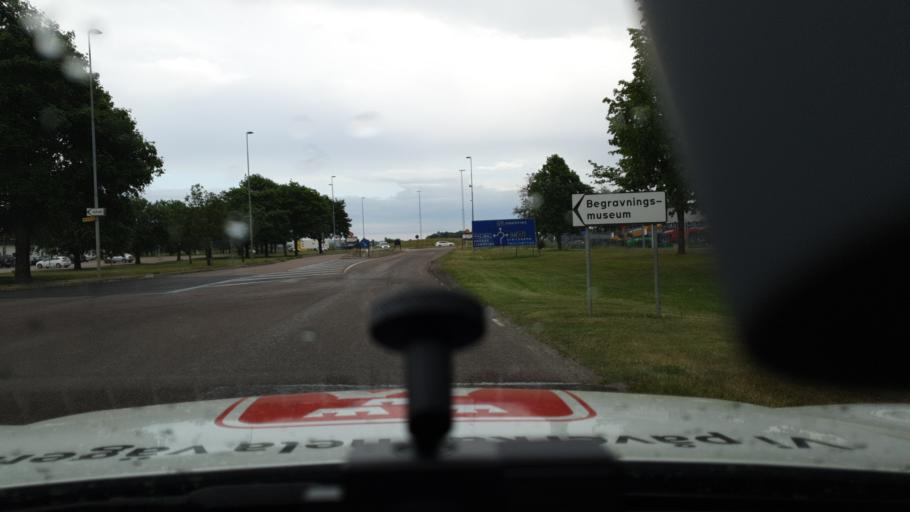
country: SE
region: Vaestra Goetaland
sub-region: Falkopings Kommun
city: Falkoeping
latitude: 58.1618
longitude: 13.5698
